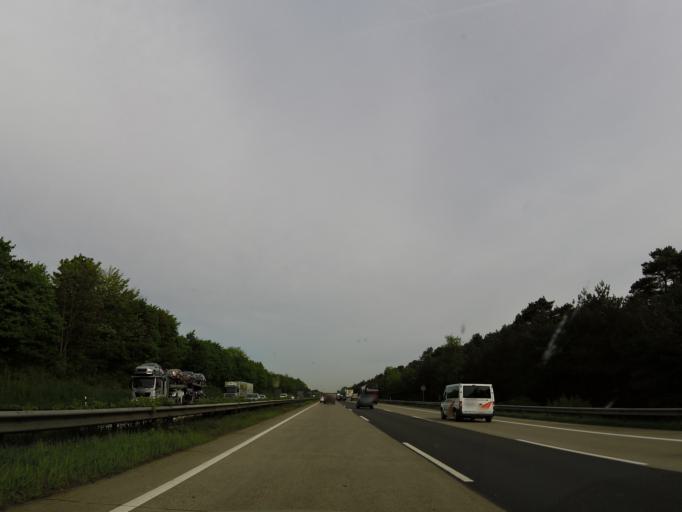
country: DE
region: Lower Saxony
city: Elze
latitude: 52.6027
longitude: 9.7443
